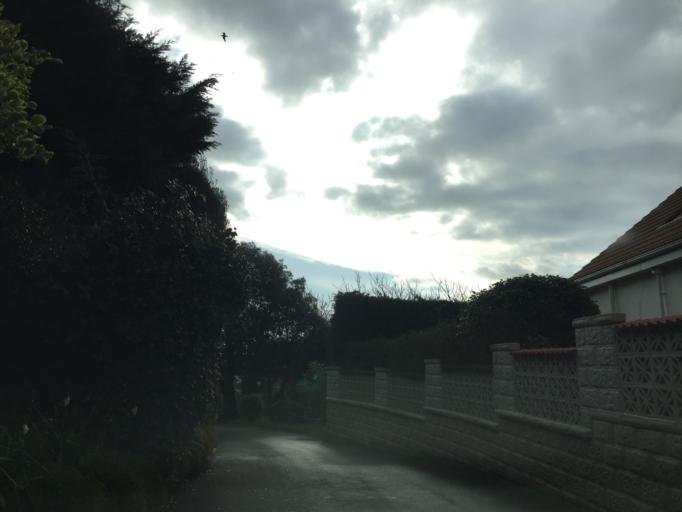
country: JE
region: St Helier
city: Saint Helier
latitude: 49.1998
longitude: -2.1380
